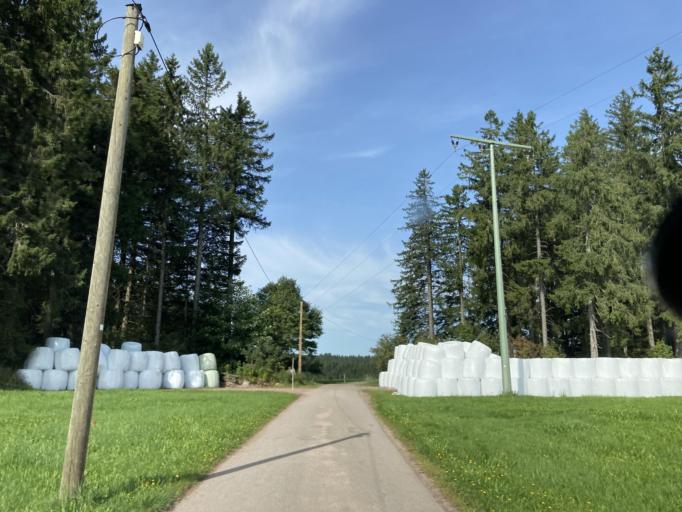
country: DE
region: Baden-Wuerttemberg
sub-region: Freiburg Region
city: Schonwald im Schwarzwald
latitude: 48.0836
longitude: 8.2274
